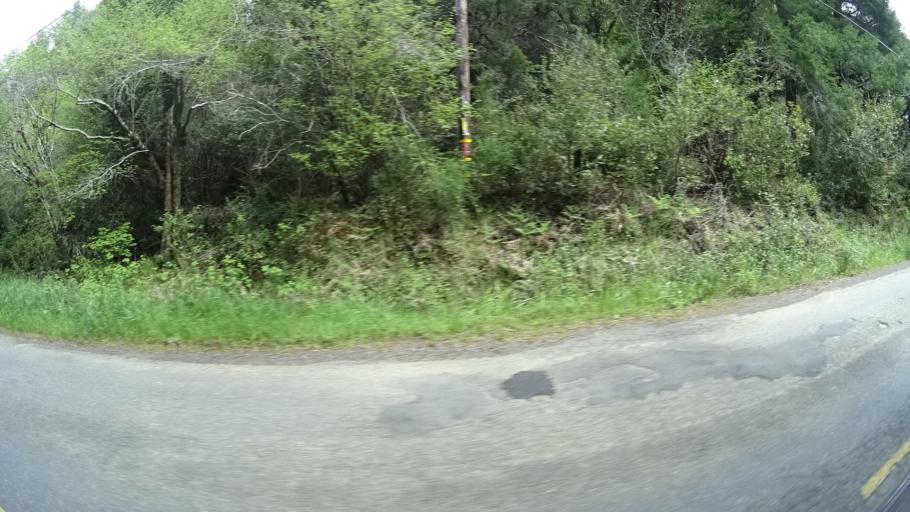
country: US
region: California
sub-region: Humboldt County
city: Redway
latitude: 40.0613
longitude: -123.9609
